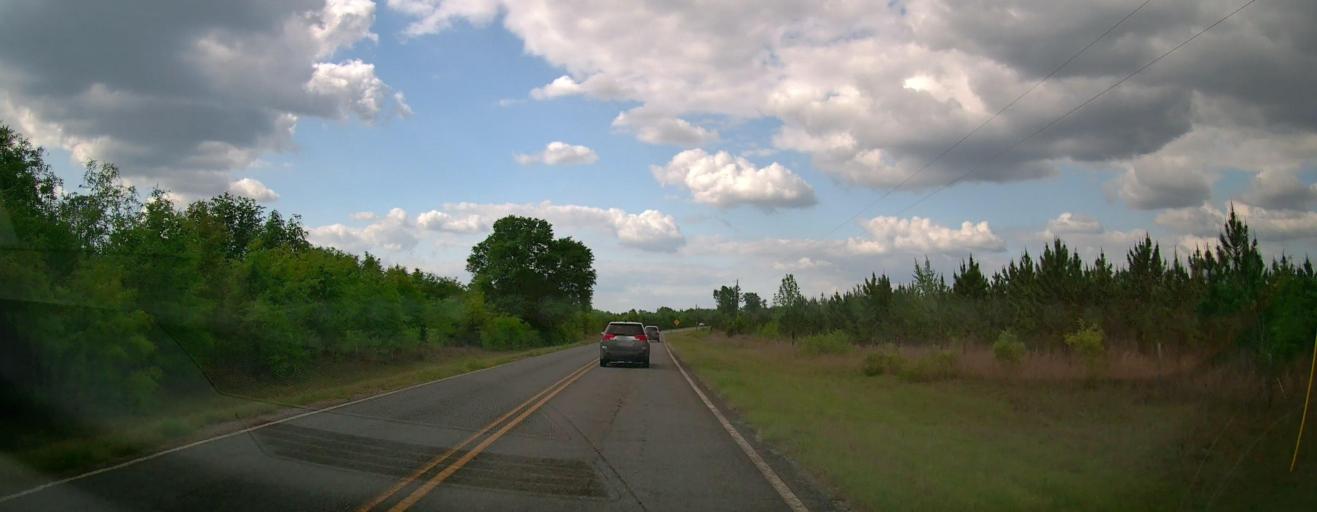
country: US
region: Georgia
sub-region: Washington County
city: Tennille
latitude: 32.7608
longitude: -82.9299
